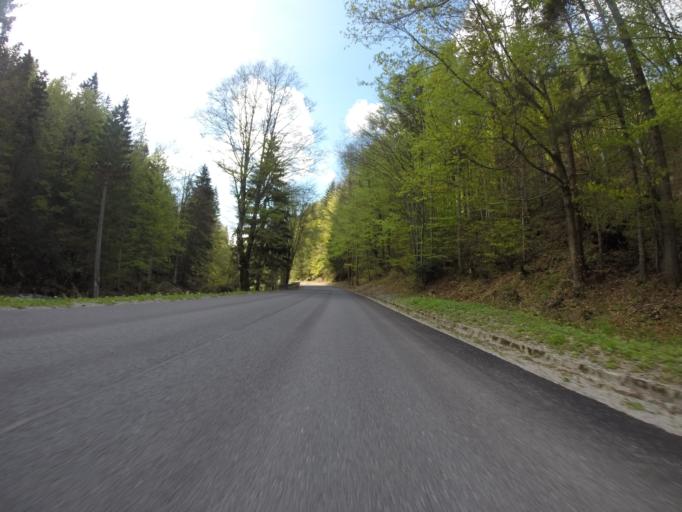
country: SK
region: Banskobystricky
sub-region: Okres Banska Bystrica
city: Brezno
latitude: 48.9007
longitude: 19.5995
